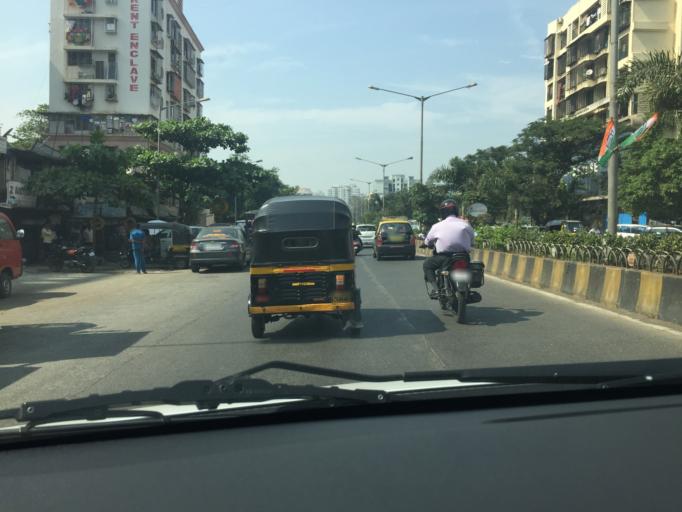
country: IN
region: Maharashtra
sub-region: Mumbai Suburban
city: Borivli
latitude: 19.2202
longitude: 72.8473
